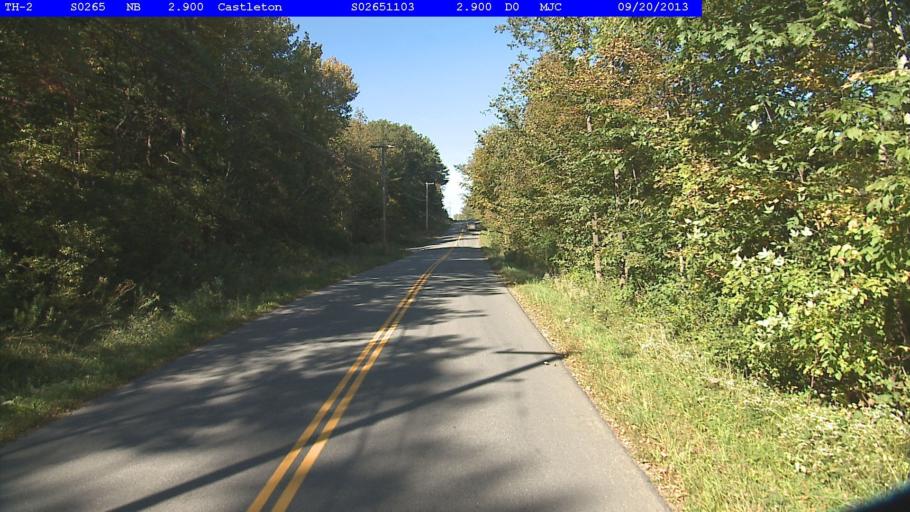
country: US
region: Vermont
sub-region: Rutland County
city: Fair Haven
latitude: 43.6426
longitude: -73.2337
